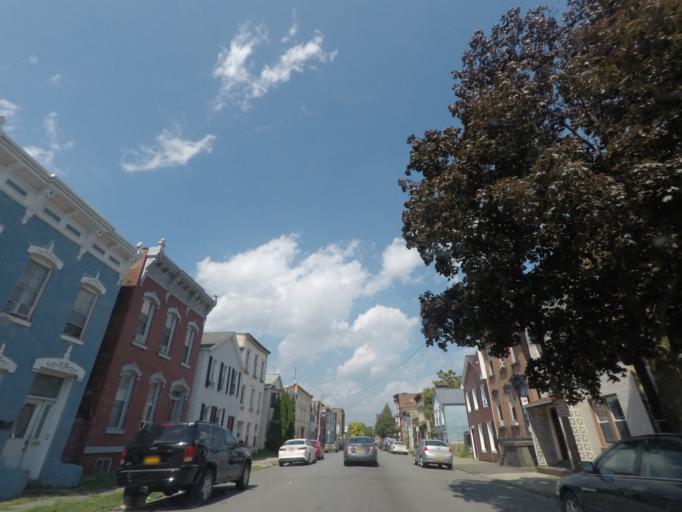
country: US
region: New York
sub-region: Rensselaer County
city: Troy
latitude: 42.7189
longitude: -73.6942
